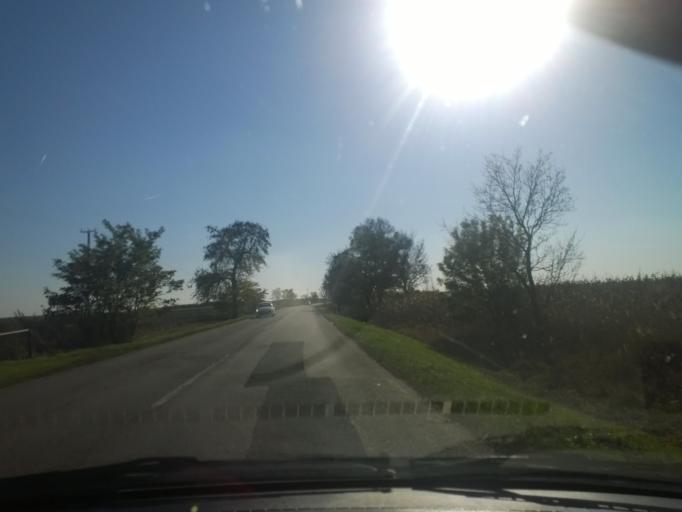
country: HU
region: Csongrad
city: Szegvar
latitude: 46.5653
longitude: 20.3125
